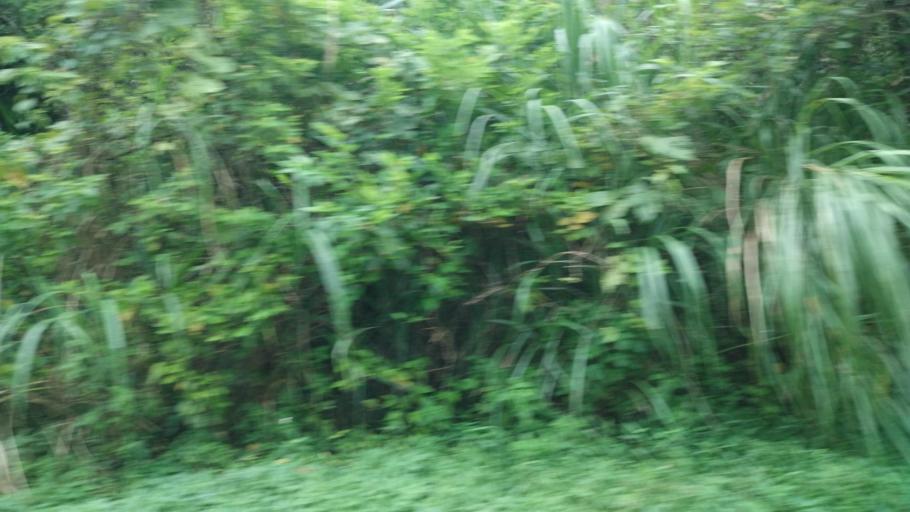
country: TW
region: Taiwan
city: Daxi
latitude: 24.9106
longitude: 121.4012
